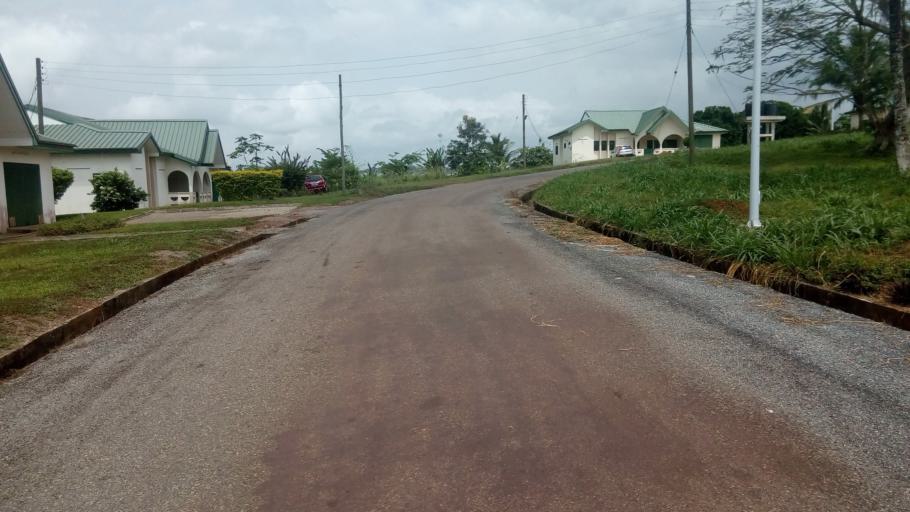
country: GH
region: Western
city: Tarkwa
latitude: 5.2955
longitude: -2.0123
